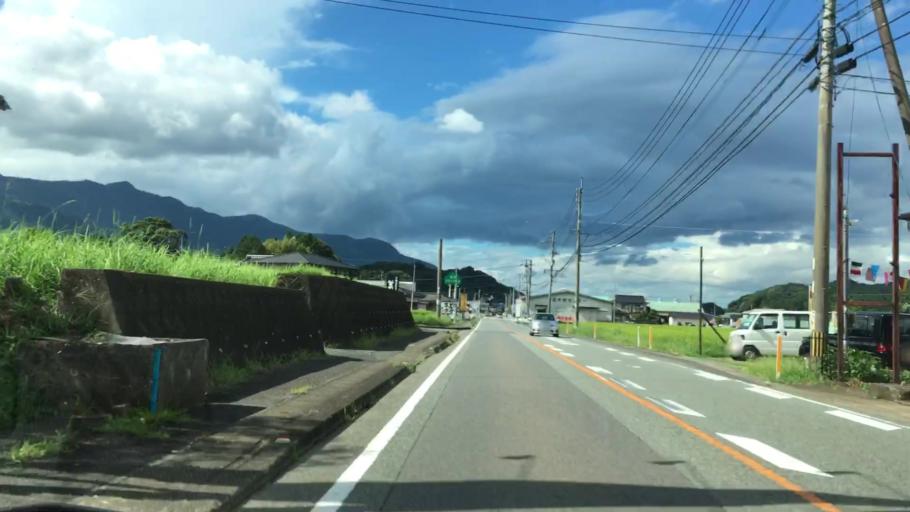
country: JP
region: Saga Prefecture
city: Imaricho-ko
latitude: 33.1894
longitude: 129.8520
